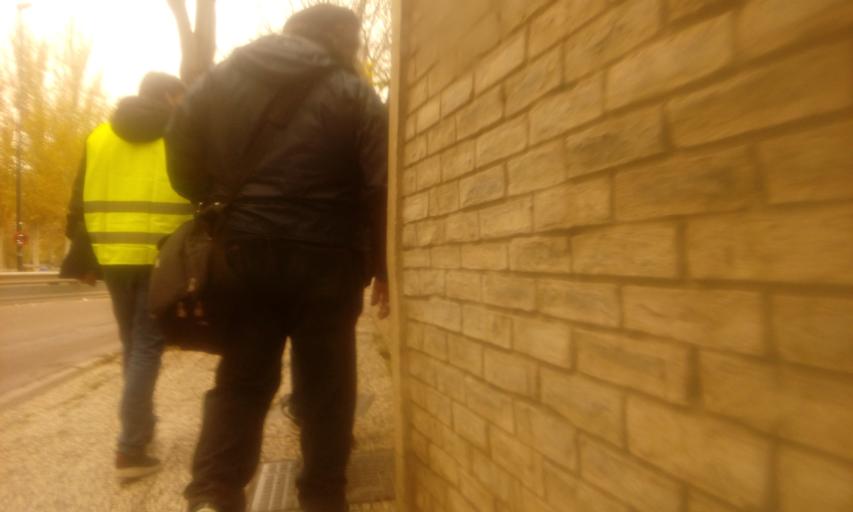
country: ES
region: Aragon
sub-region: Provincia de Zaragoza
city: Zaragoza
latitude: 41.6513
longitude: -0.8702
